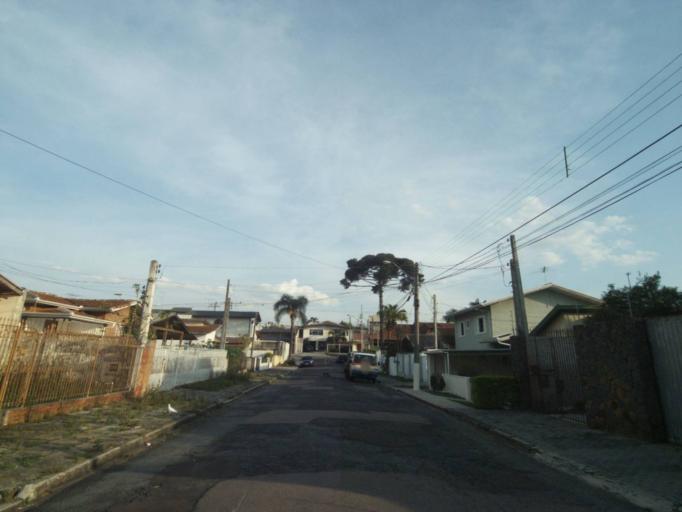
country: BR
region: Parana
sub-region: Curitiba
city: Curitiba
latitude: -25.4541
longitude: -49.3103
